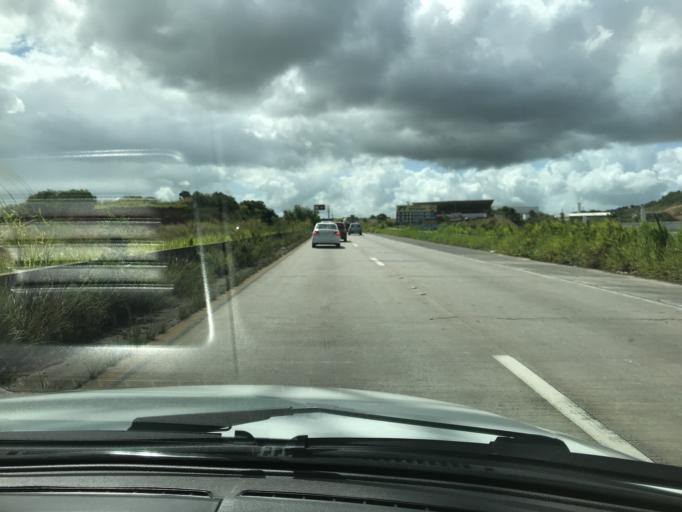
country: BR
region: Pernambuco
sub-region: Vitoria De Santo Antao
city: Vitoria de Santo Antao
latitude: -8.1207
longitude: -35.2661
